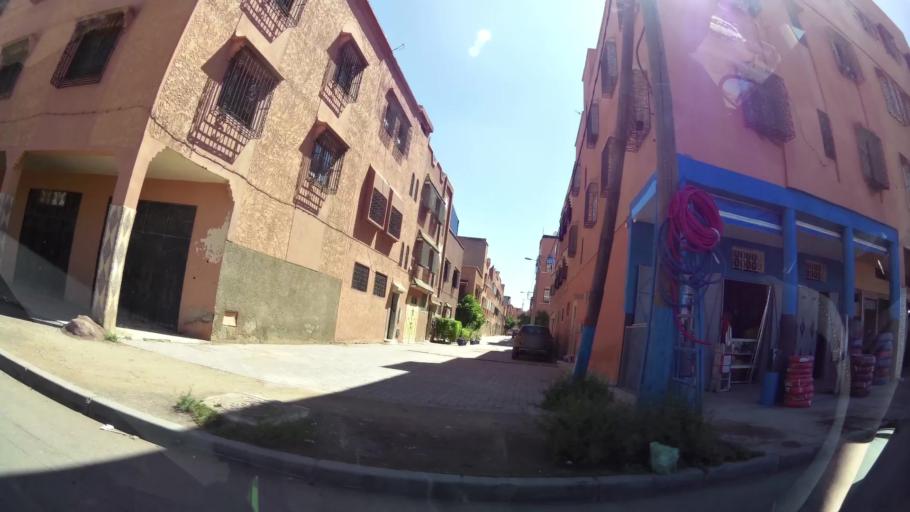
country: MA
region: Marrakech-Tensift-Al Haouz
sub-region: Marrakech
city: Marrakesh
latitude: 31.6309
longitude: -8.0703
